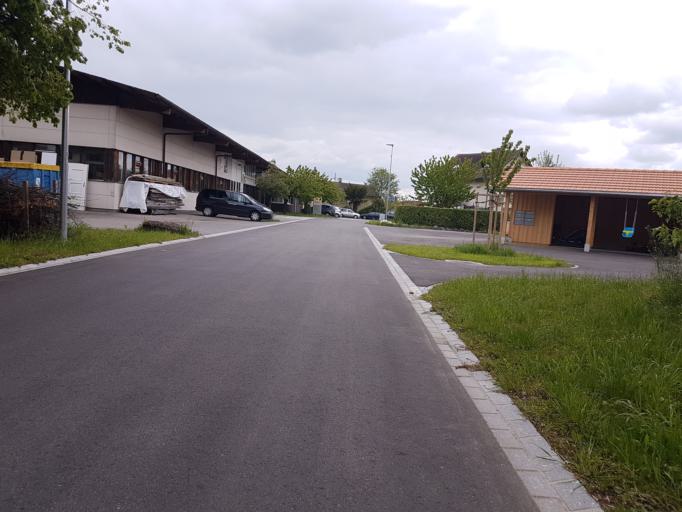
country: CH
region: Solothurn
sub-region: Bezirk Wasseramt
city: Deitingen
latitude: 47.2244
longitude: 7.6163
